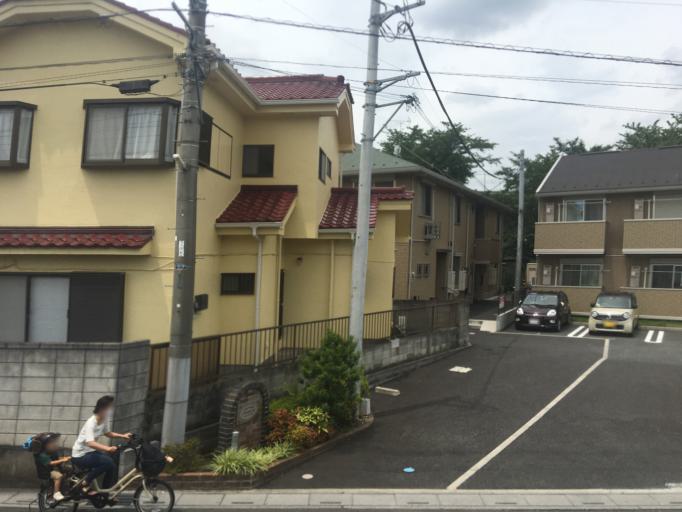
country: JP
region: Saitama
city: Koshigaya
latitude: 35.9314
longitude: 139.7757
